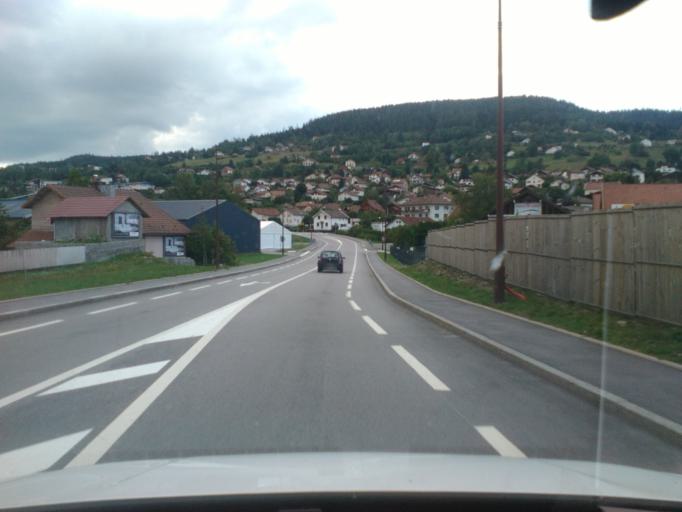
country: FR
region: Lorraine
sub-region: Departement des Vosges
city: Gerardmer
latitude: 48.0780
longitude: 6.8855
